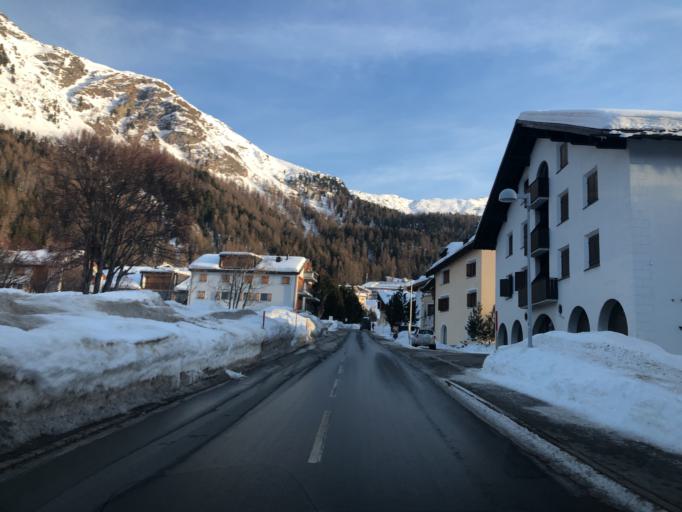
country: CH
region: Grisons
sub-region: Maloja District
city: Silvaplana
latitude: 46.4589
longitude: 9.8107
